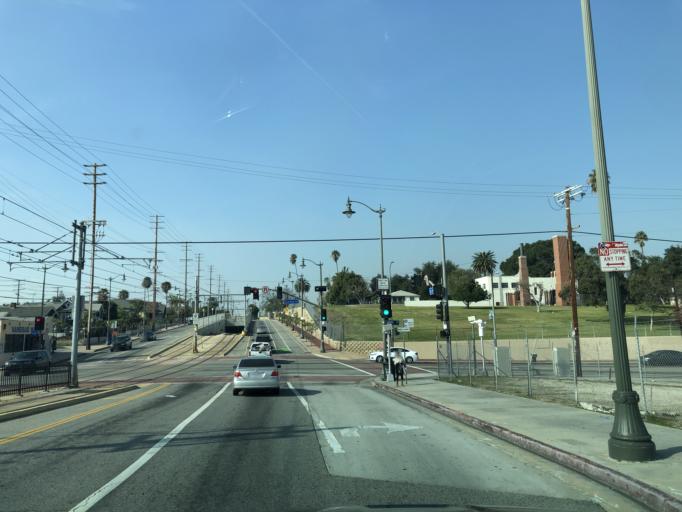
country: US
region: California
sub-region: Los Angeles County
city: Boyle Heights
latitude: 34.0370
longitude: -118.1945
